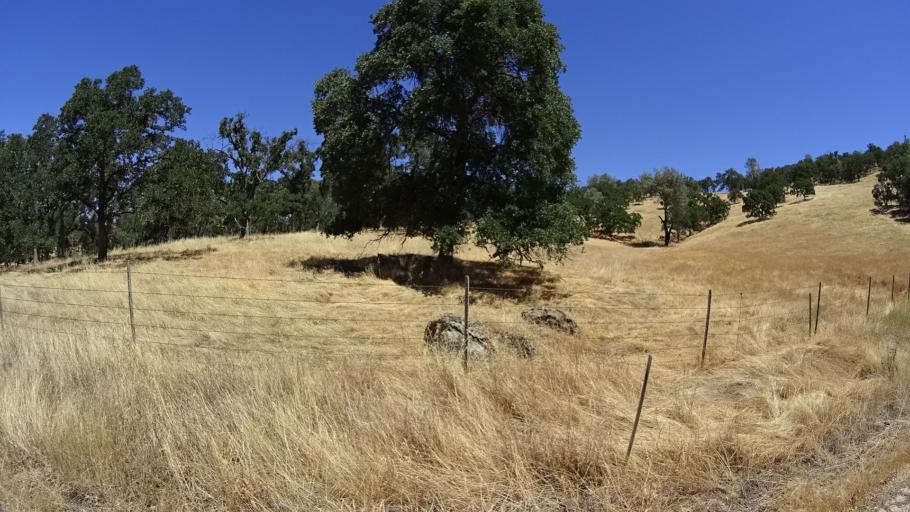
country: US
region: California
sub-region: Calaveras County
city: Rancho Calaveras
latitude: 38.0504
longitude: -120.7942
